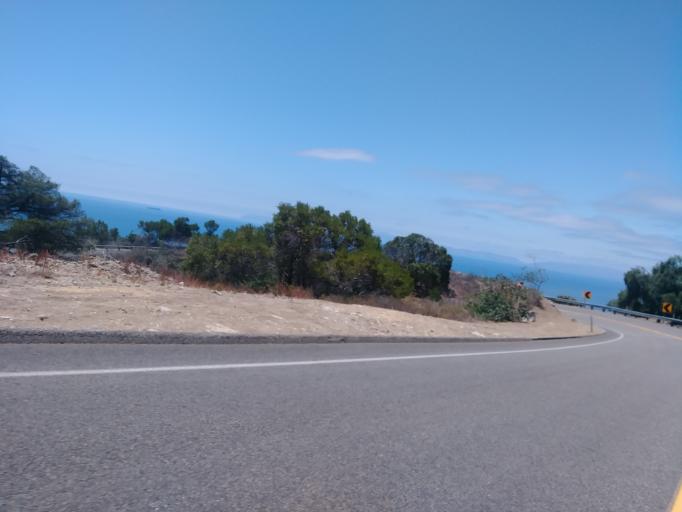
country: US
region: California
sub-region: Los Angeles County
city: Rolling Hills
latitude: 33.7304
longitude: -118.3310
